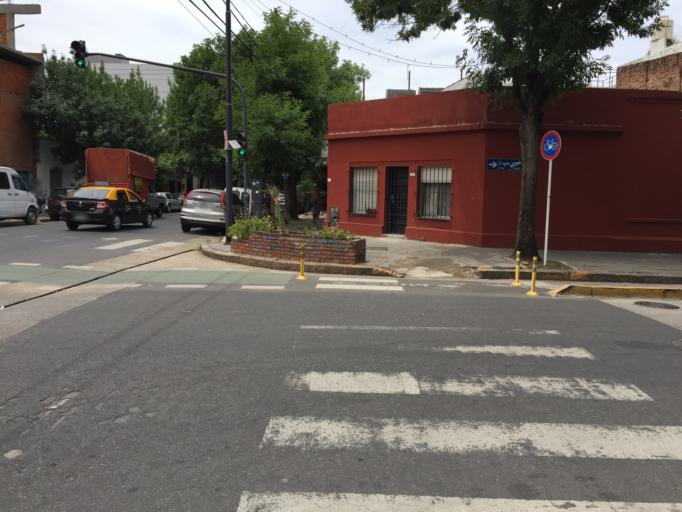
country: AR
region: Buenos Aires F.D.
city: Colegiales
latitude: -34.5884
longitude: -58.4433
